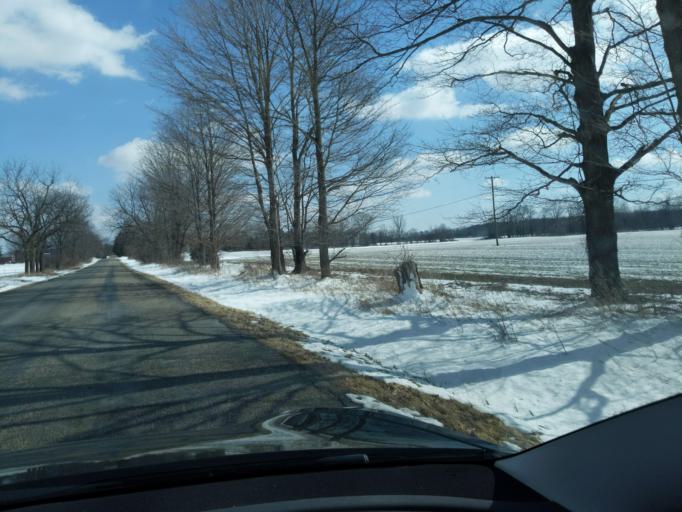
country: US
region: Michigan
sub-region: Ingham County
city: Mason
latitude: 42.6109
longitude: -84.3770
